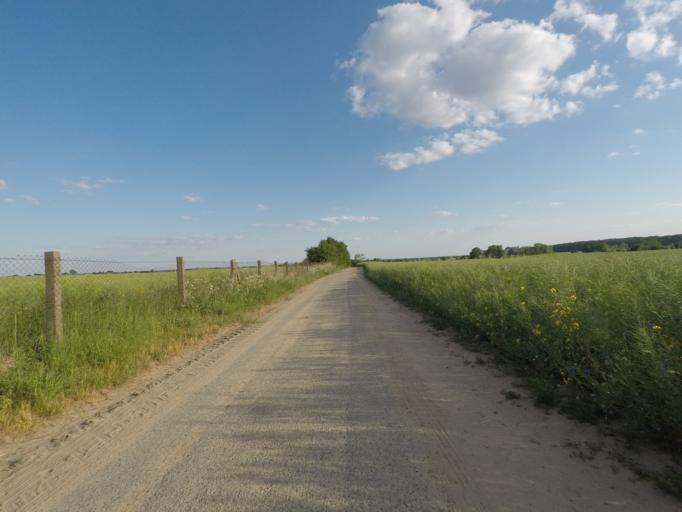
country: DE
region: Brandenburg
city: Britz
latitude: 52.8789
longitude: 13.7281
